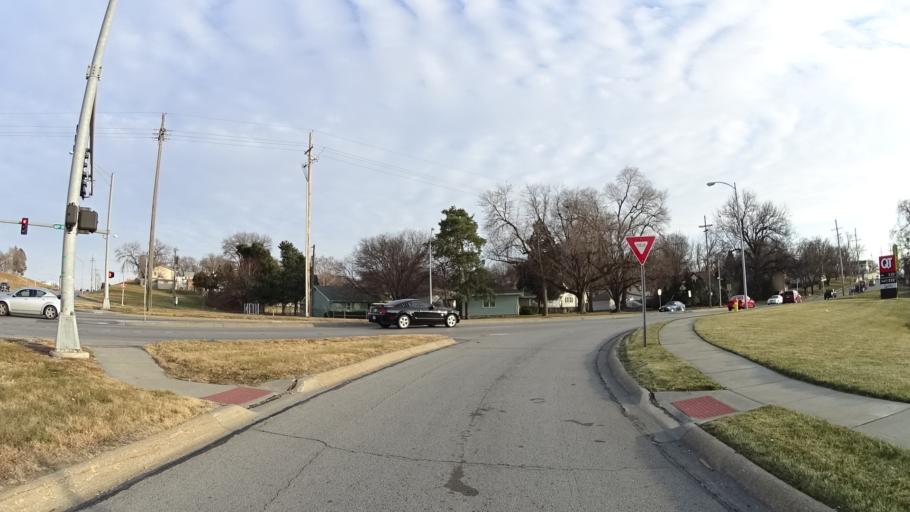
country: US
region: Nebraska
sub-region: Douglas County
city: Ralston
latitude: 41.2123
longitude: -96.0050
